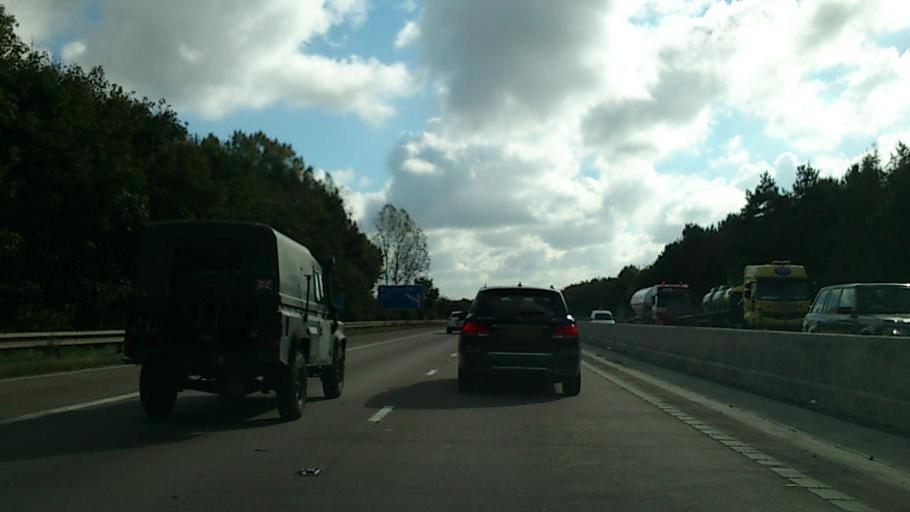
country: GB
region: England
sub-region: Shropshire
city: Tong
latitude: 52.6677
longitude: -2.3296
